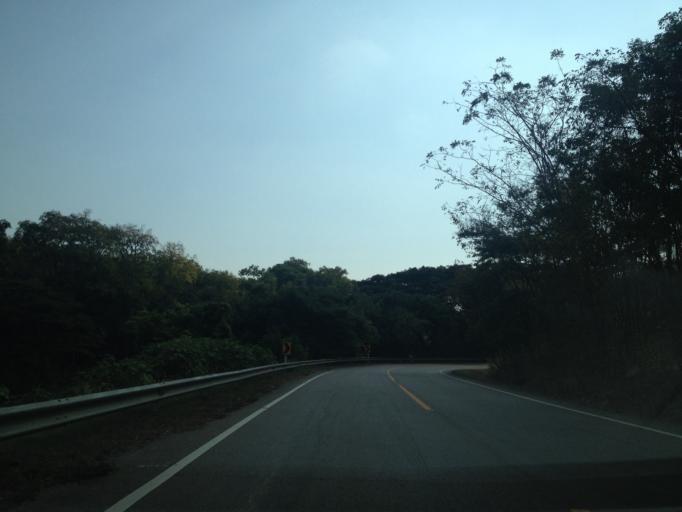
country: TH
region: Chiang Mai
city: Hot
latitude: 18.2307
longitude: 98.5584
